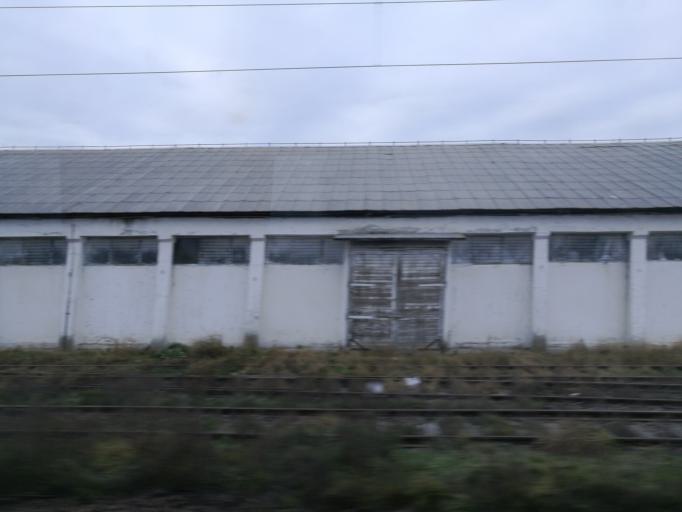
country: RO
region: Neamt
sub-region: Comuna Secueni
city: Secueni
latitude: 46.8489
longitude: 26.8812
